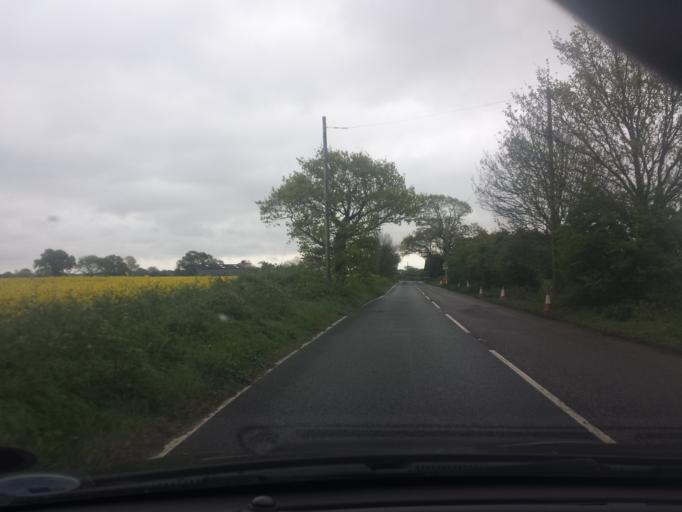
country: GB
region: England
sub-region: Essex
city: Mistley
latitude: 51.9303
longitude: 1.1432
